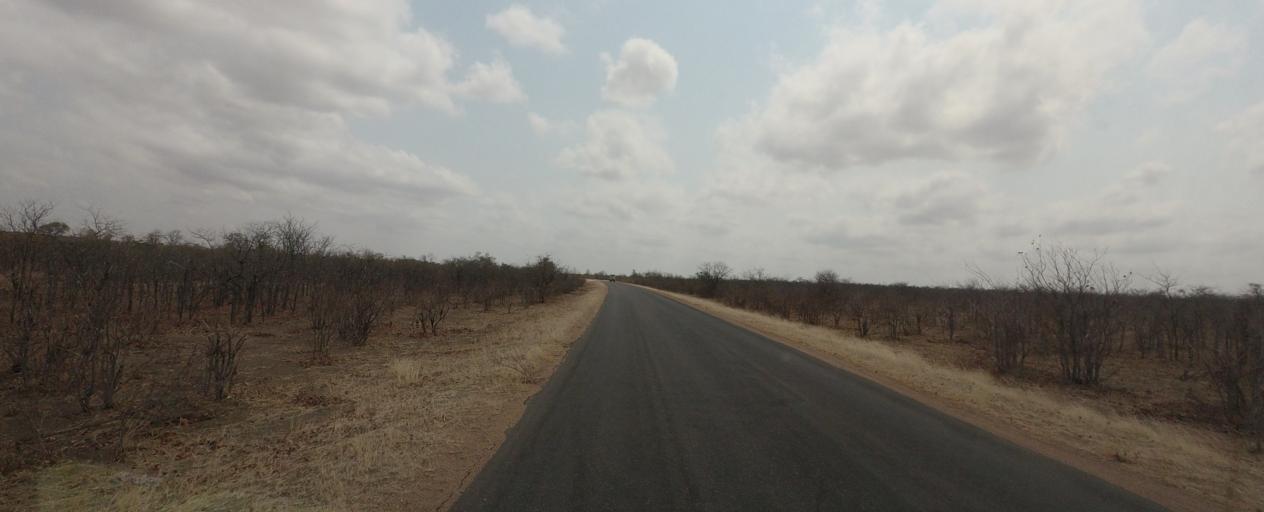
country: ZA
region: Limpopo
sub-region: Mopani District Municipality
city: Phalaborwa
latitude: -23.5973
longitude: 31.4550
